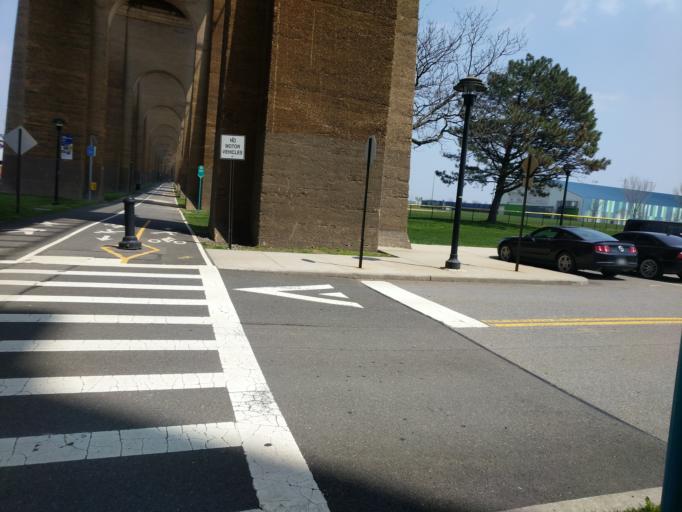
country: US
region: New York
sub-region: New York County
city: Manhattan
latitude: 40.7929
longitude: -73.9220
